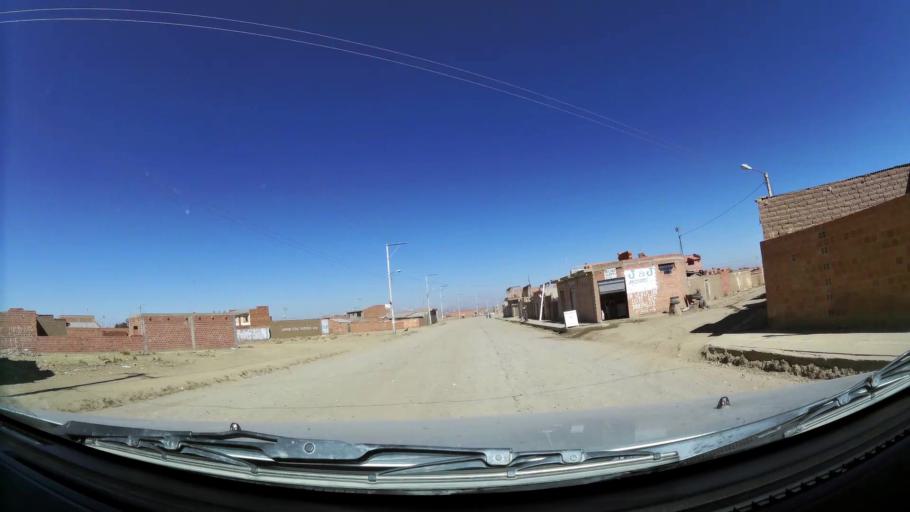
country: BO
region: La Paz
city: La Paz
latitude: -16.6228
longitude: -68.1886
